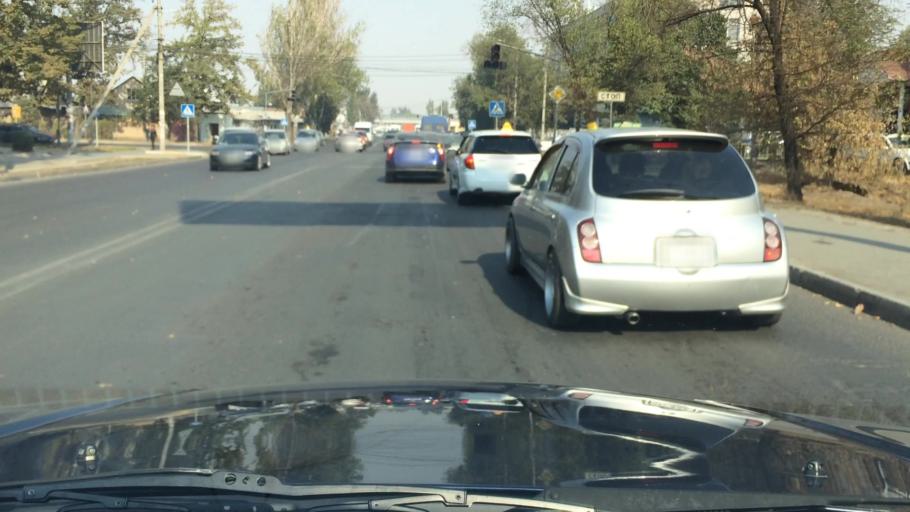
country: KG
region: Chuy
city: Lebedinovka
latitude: 42.8829
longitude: 74.6367
